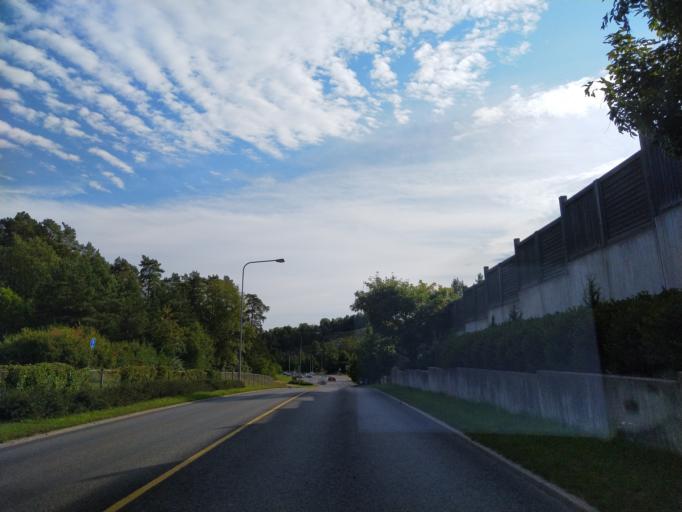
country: FI
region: Varsinais-Suomi
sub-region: Turku
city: Turku
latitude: 60.4198
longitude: 22.2322
